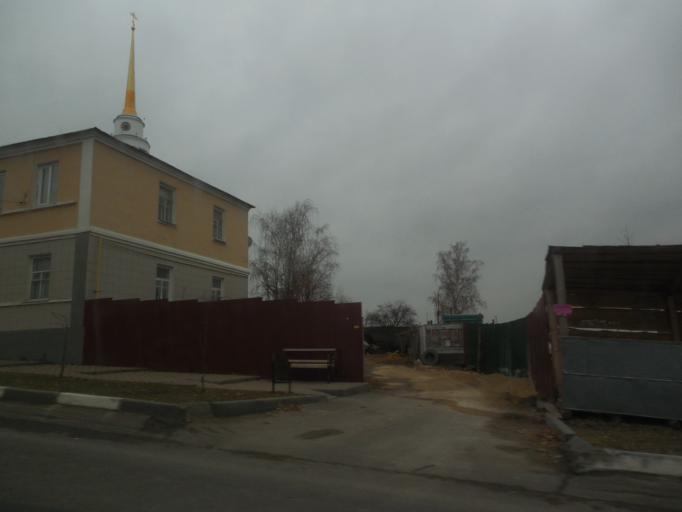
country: RU
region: Lipetsk
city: Zadonsk
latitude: 52.3933
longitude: 38.9168
